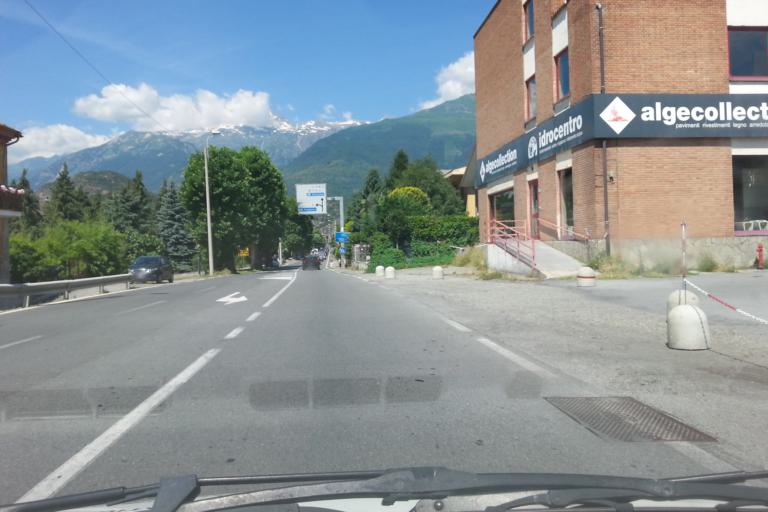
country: IT
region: Piedmont
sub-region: Provincia di Torino
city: Susa
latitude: 45.1366
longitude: 7.0652
